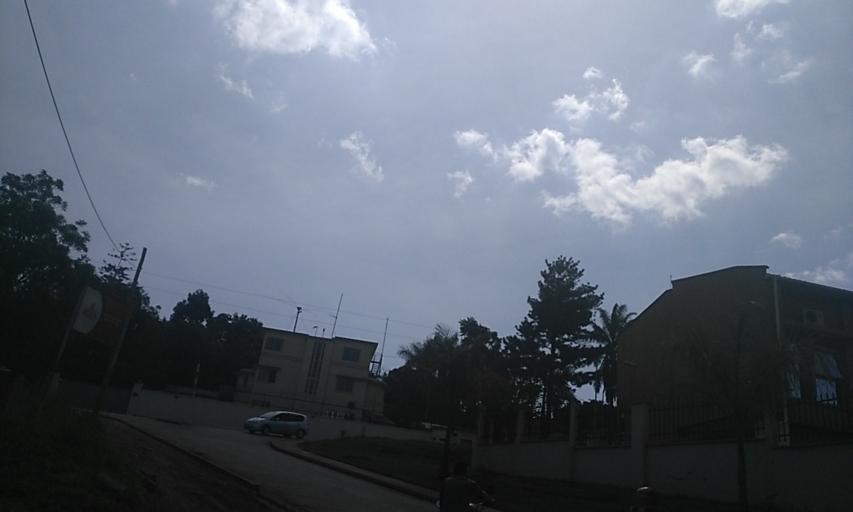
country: UG
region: Central Region
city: Kampala Central Division
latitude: 0.3314
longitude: 32.5802
